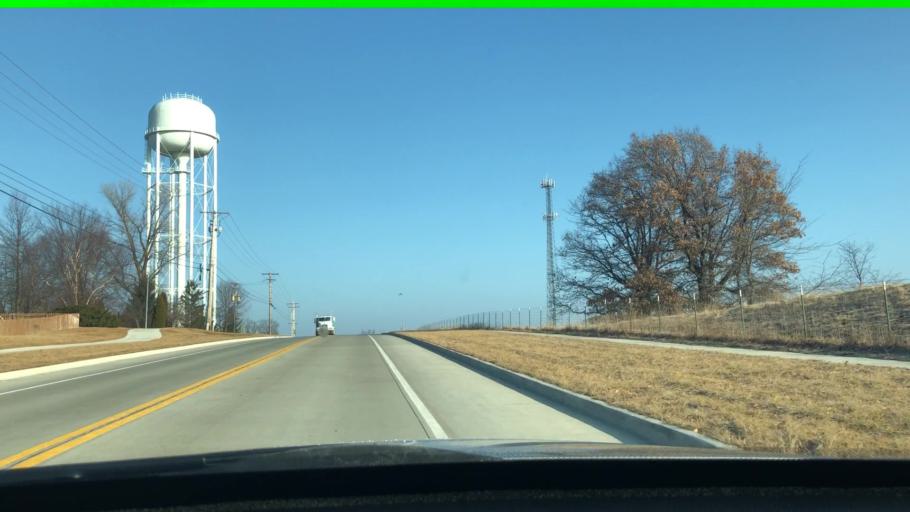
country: US
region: Missouri
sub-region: Boone County
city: Columbia
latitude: 38.8950
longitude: -92.4005
